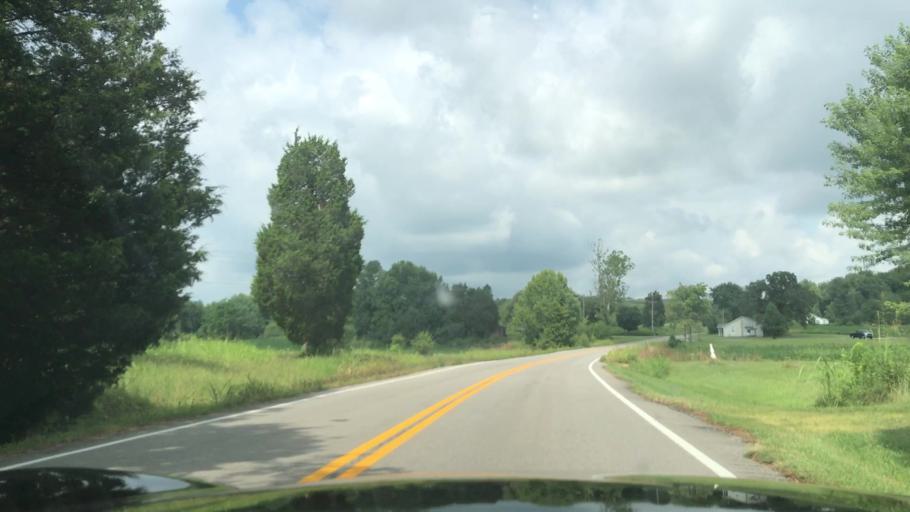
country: US
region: Kentucky
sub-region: Muhlenberg County
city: Central City
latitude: 37.1953
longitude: -86.9913
